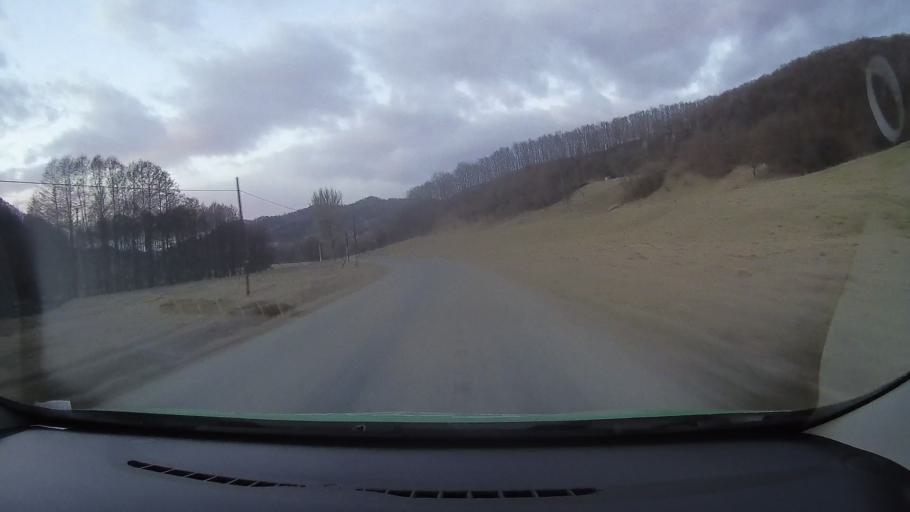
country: RO
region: Dambovita
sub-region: Comuna Valea Lunga
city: Valea Lunga-Cricov
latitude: 45.0917
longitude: 25.5796
